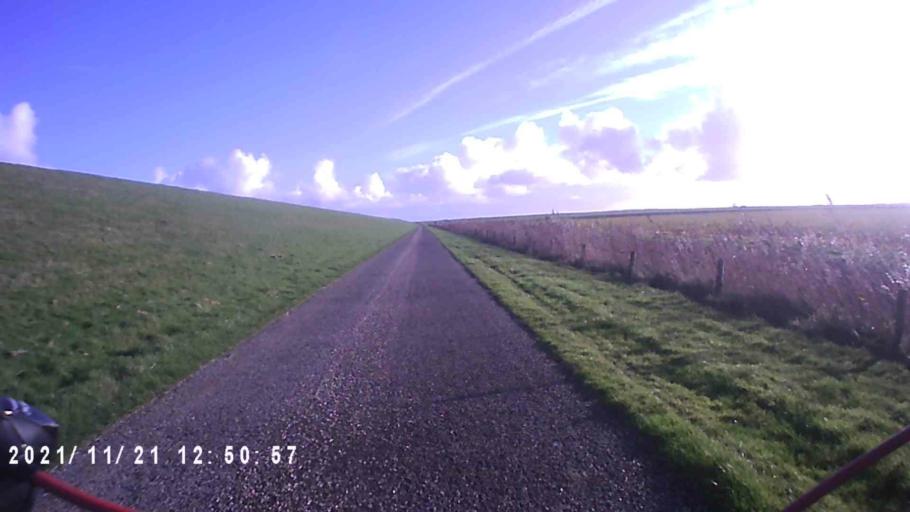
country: NL
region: Friesland
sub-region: Gemeente Dongeradeel
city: Anjum
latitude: 53.4009
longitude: 6.1224
